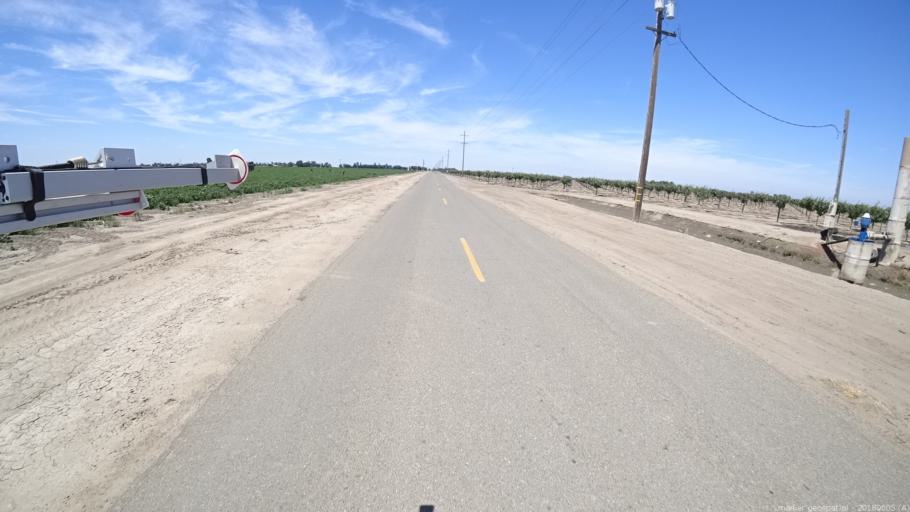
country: US
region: California
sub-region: Merced County
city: Dos Palos
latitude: 37.0871
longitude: -120.4735
